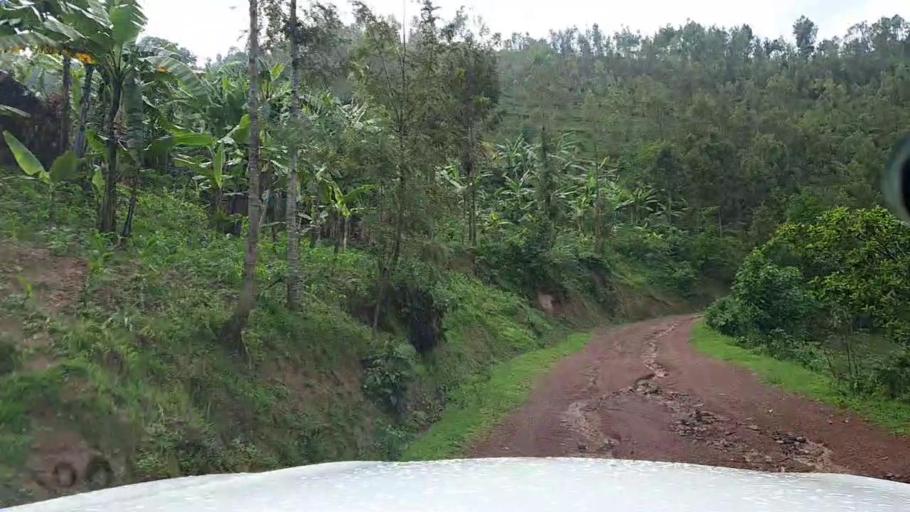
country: RW
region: Northern Province
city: Byumba
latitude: -1.7232
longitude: 29.9176
